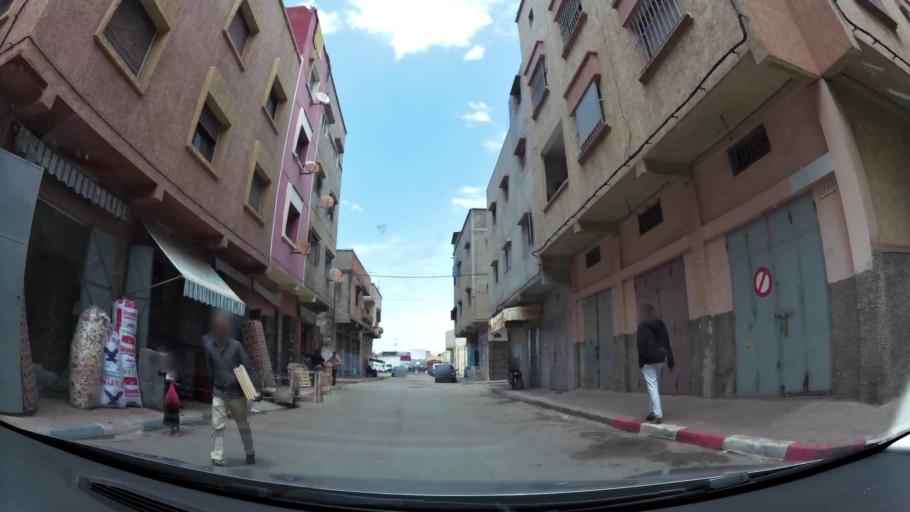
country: MA
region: Rabat-Sale-Zemmour-Zaer
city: Sale
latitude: 34.0547
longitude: -6.8206
